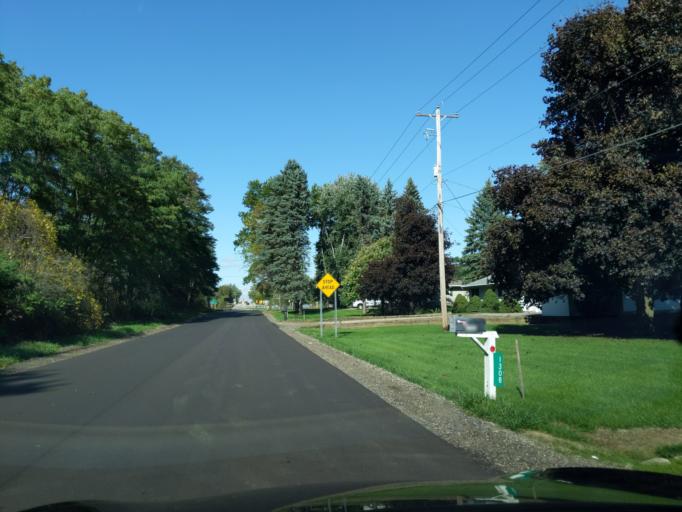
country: US
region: Michigan
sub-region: Eaton County
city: Charlotte
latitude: 42.5865
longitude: -84.7978
